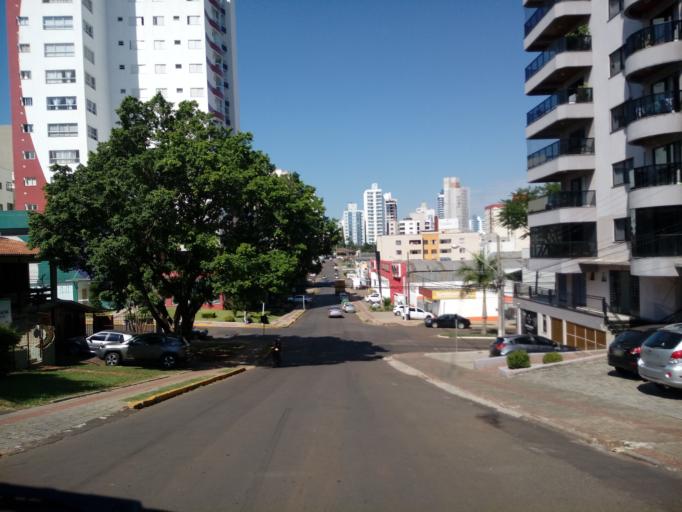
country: BR
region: Santa Catarina
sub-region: Chapeco
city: Chapeco
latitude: -27.0963
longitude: -52.6115
